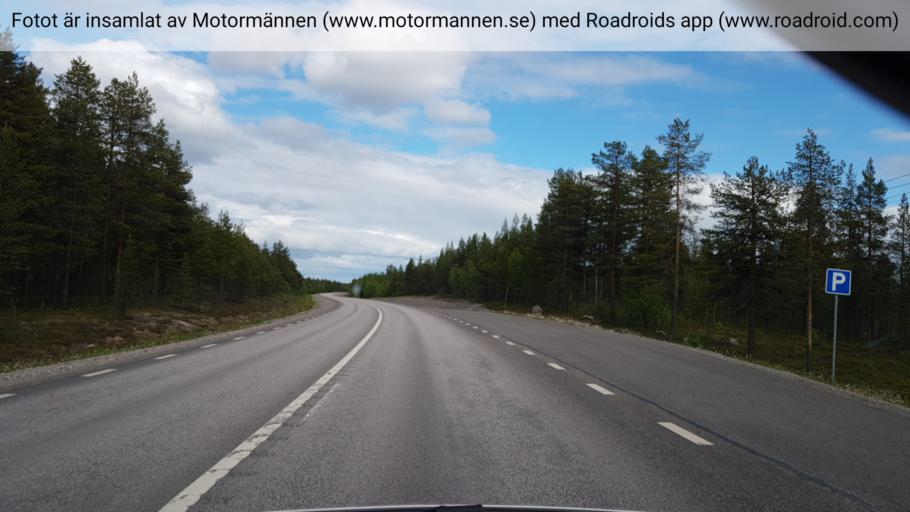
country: SE
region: Norrbotten
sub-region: Gallivare Kommun
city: Malmberget
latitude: 67.6623
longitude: 21.4436
